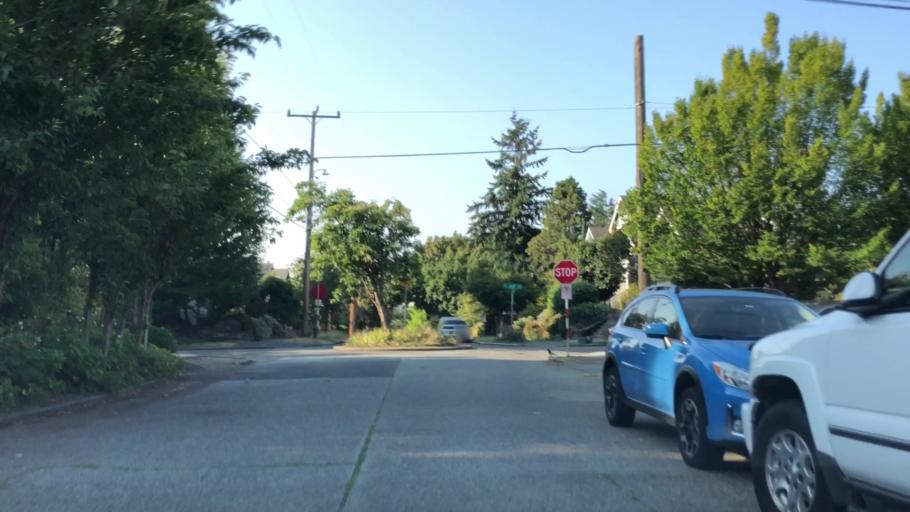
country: US
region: Washington
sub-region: King County
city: Seattle
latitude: 47.6607
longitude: -122.3338
